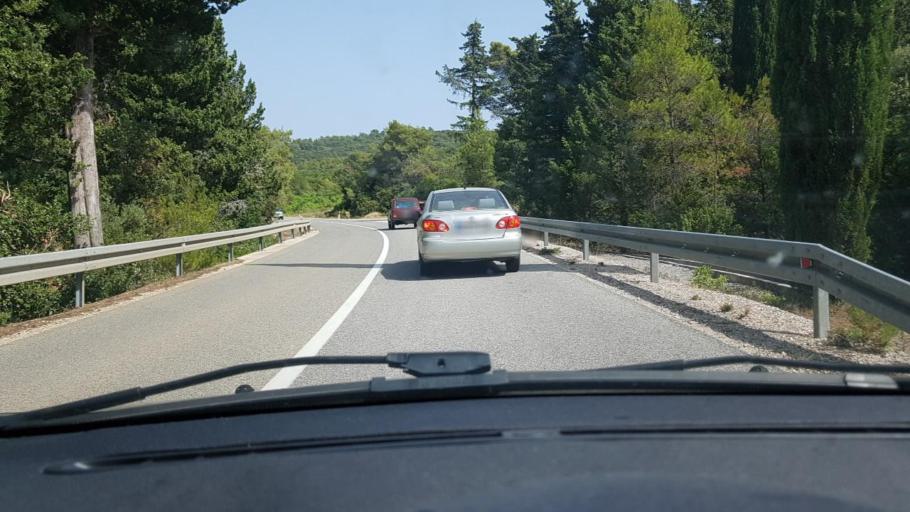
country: HR
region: Dubrovacko-Neretvanska
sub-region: Grad Korcula
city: Zrnovo
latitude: 42.9369
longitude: 17.0807
